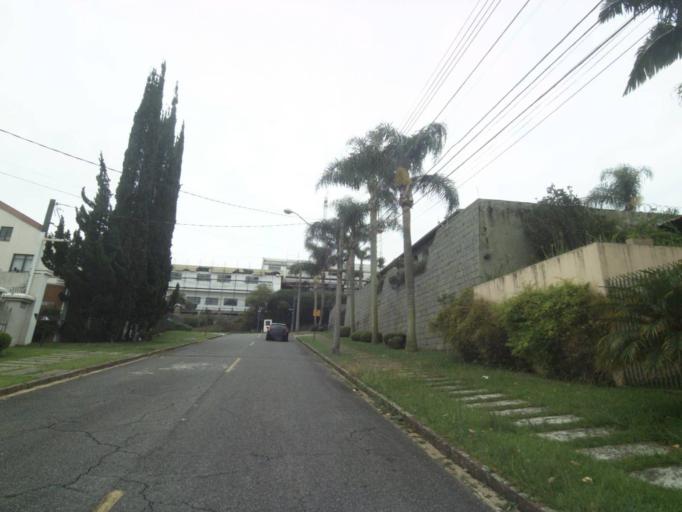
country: BR
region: Parana
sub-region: Curitiba
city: Curitiba
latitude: -25.4059
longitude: -49.2885
